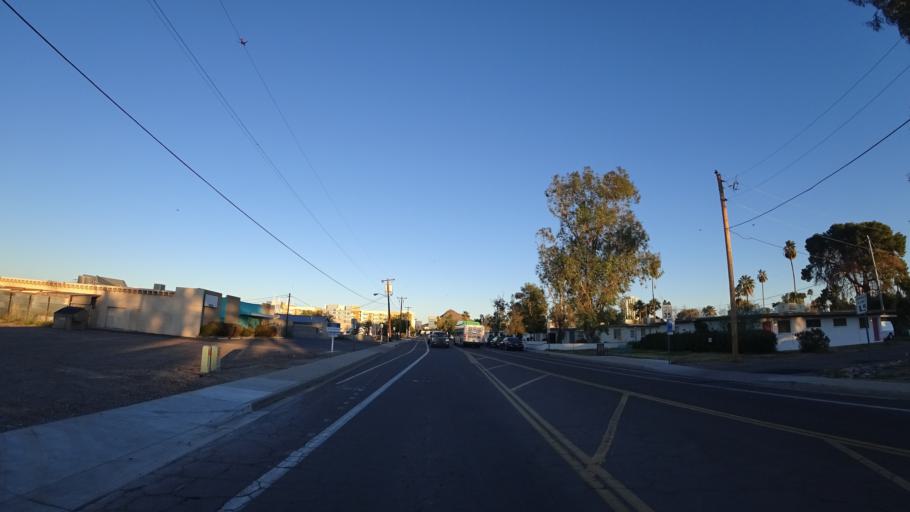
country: US
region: Arizona
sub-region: Maricopa County
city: Tempe Junction
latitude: 33.4291
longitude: -111.9520
